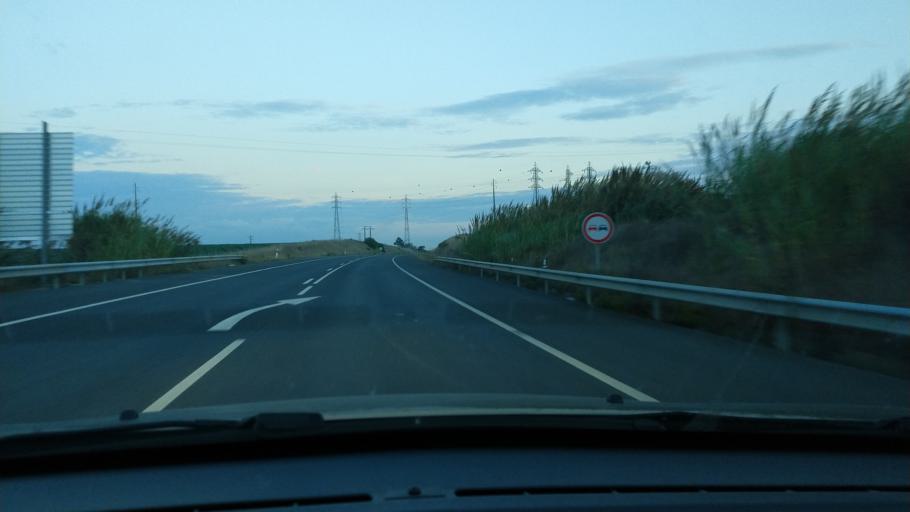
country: PT
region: Leiria
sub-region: Peniche
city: Atouguia da Baleia
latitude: 39.3286
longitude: -9.3207
